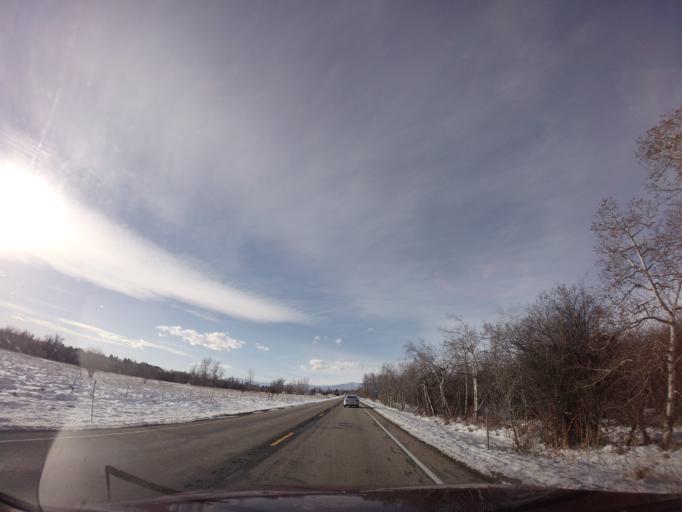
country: US
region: Montana
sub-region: Carbon County
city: Red Lodge
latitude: 45.3668
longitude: -109.1618
